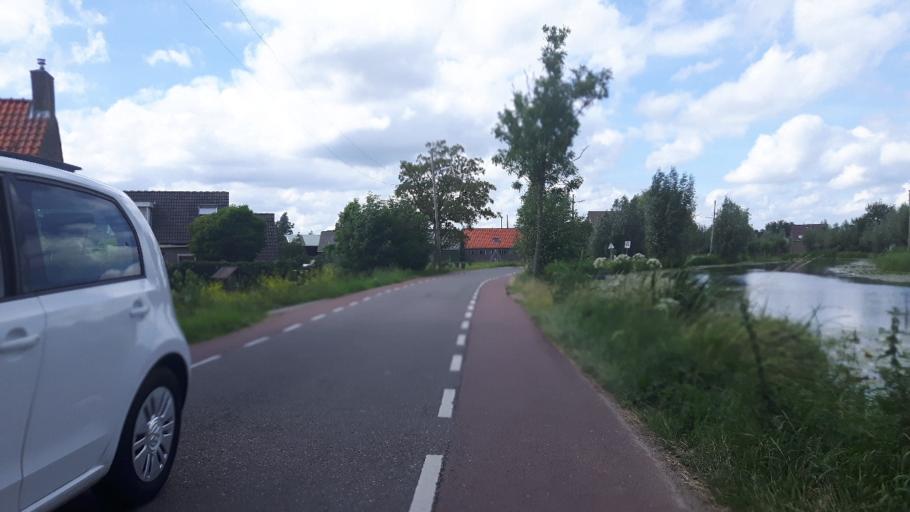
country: NL
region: South Holland
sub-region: Gemeente Vlist
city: Vlist
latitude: 51.9759
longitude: 4.8220
